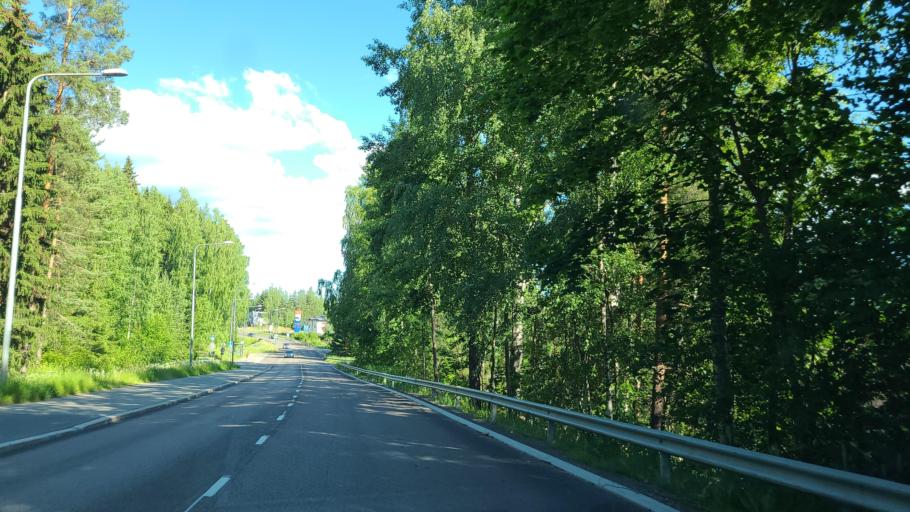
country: FI
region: Central Finland
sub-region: Jyvaeskylae
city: Jyvaeskylae
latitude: 62.2418
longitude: 25.8015
